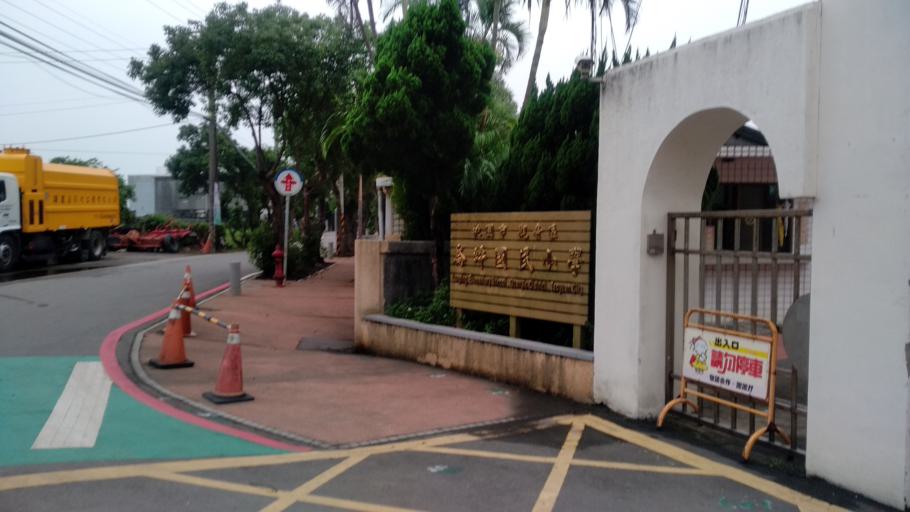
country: TW
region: Taiwan
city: Taoyuan City
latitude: 25.0000
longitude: 121.1629
